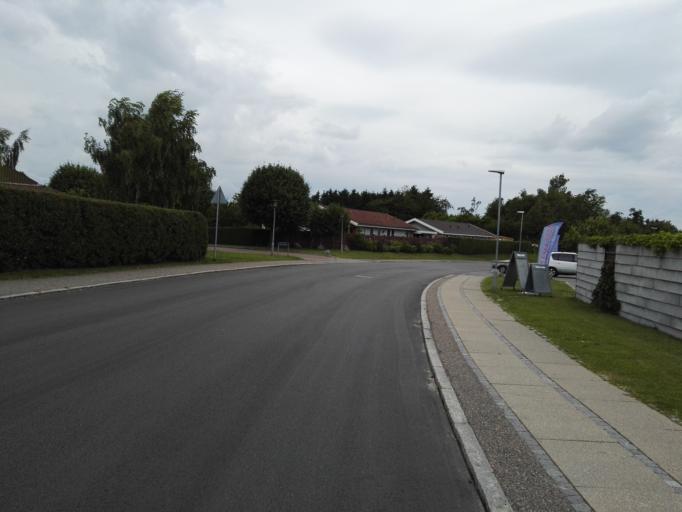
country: DK
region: Capital Region
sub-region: Egedal Kommune
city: Vekso
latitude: 55.7575
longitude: 12.2327
